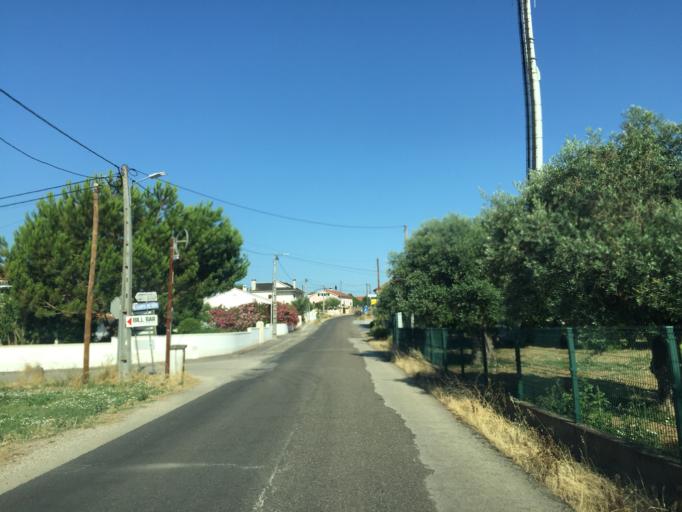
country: PT
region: Santarem
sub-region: Tomar
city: Tomar
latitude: 39.5957
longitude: -8.3744
